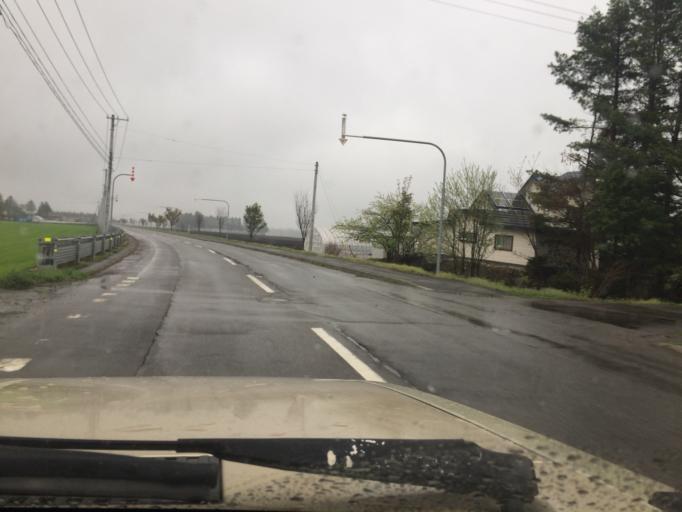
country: JP
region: Hokkaido
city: Obihiro
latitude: 42.8725
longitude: 143.0252
